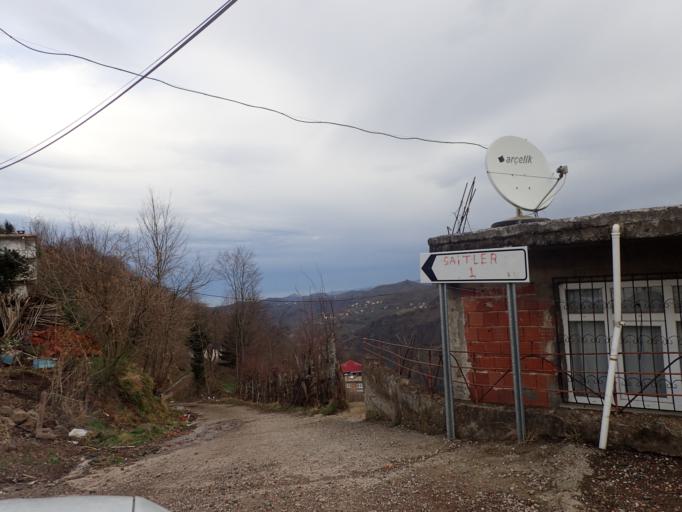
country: TR
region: Ordu
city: Camas
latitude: 40.8836
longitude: 37.5804
